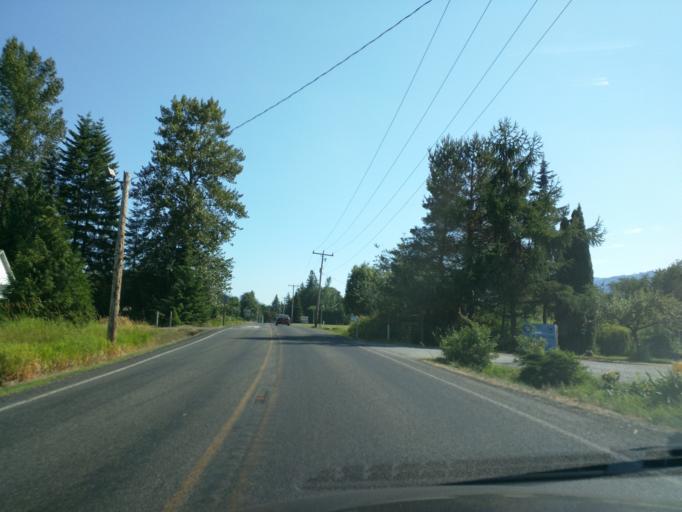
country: US
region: Washington
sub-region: Whatcom County
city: Peaceful Valley
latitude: 48.7888
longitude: -122.1919
